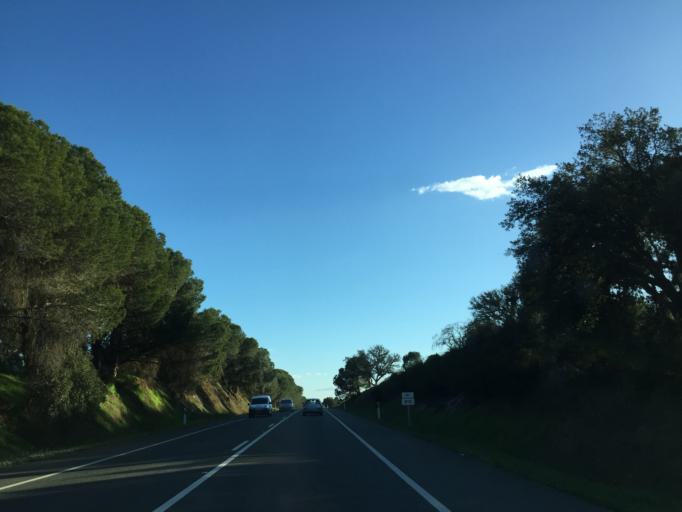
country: PT
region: Setubal
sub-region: Grandola
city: Grandola
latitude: 38.0866
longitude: -8.4177
